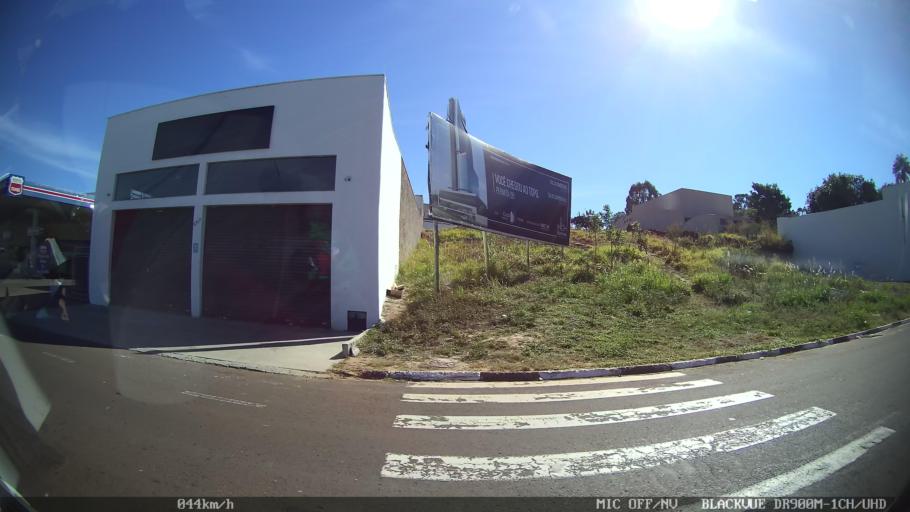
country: BR
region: Sao Paulo
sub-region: Franca
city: Franca
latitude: -20.5208
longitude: -47.3809
